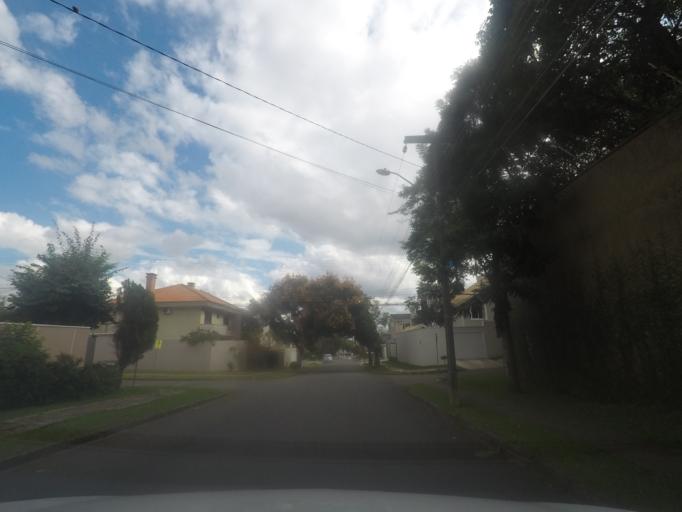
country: BR
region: Parana
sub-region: Pinhais
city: Pinhais
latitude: -25.4707
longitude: -49.2223
